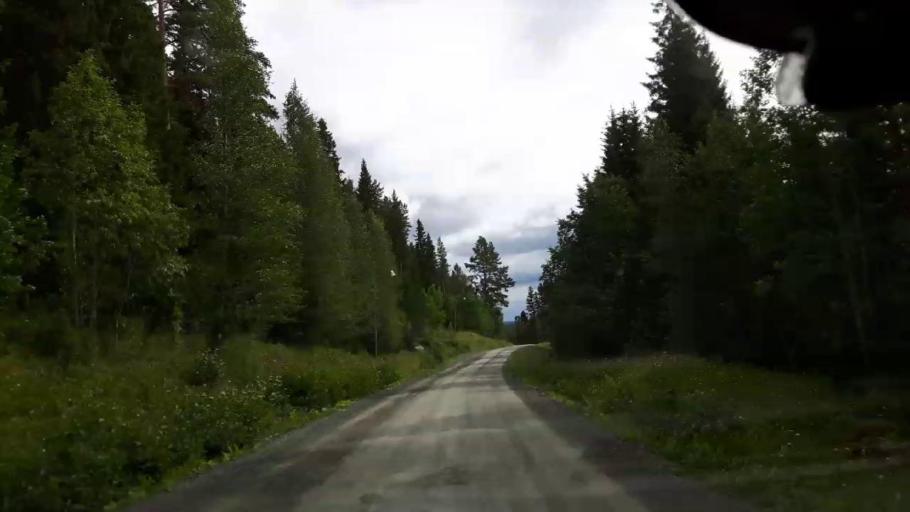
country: SE
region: Jaemtland
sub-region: Krokoms Kommun
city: Valla
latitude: 63.6206
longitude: 14.0607
